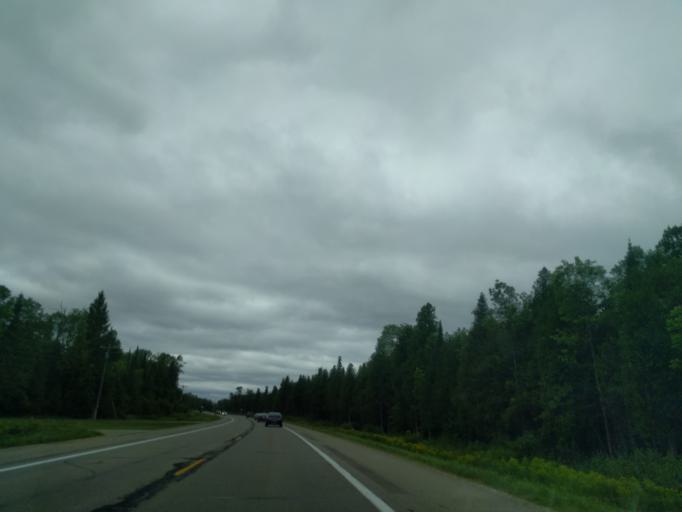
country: US
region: Michigan
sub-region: Delta County
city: Escanaba
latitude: 45.6489
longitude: -87.1849
